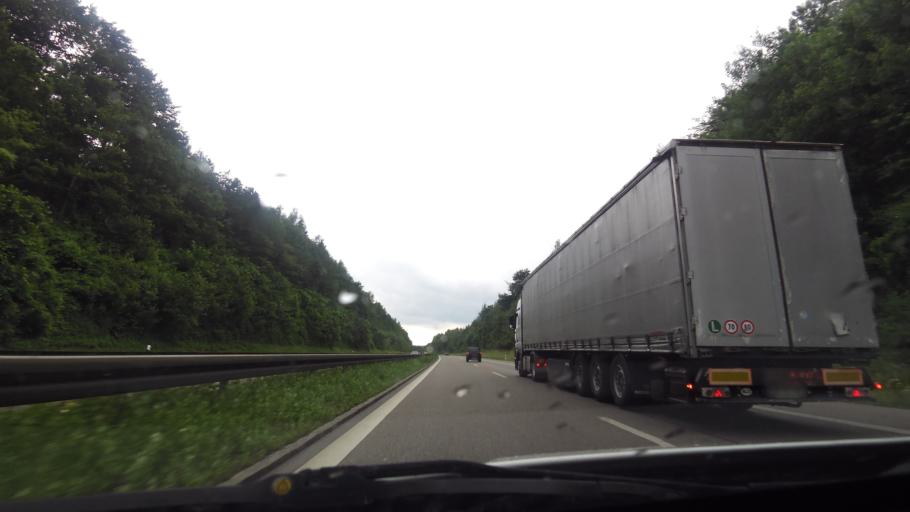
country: DE
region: Bavaria
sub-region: Swabia
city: Buxheim
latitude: 47.9854
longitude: 10.1302
